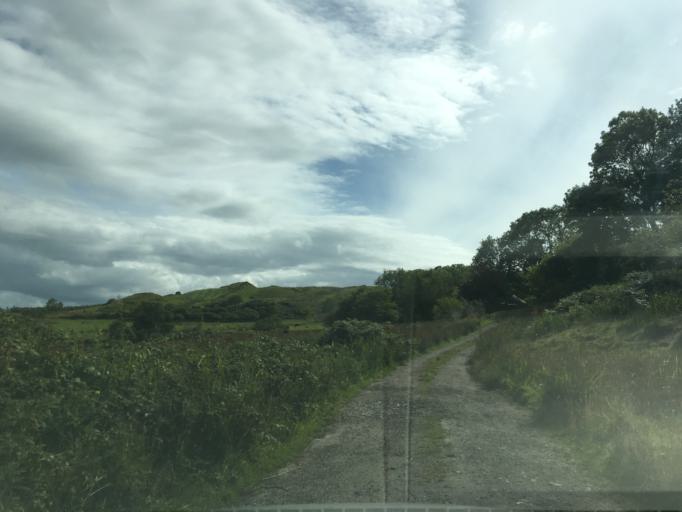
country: GB
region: Scotland
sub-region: Argyll and Bute
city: Oban
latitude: 56.2481
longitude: -5.6233
